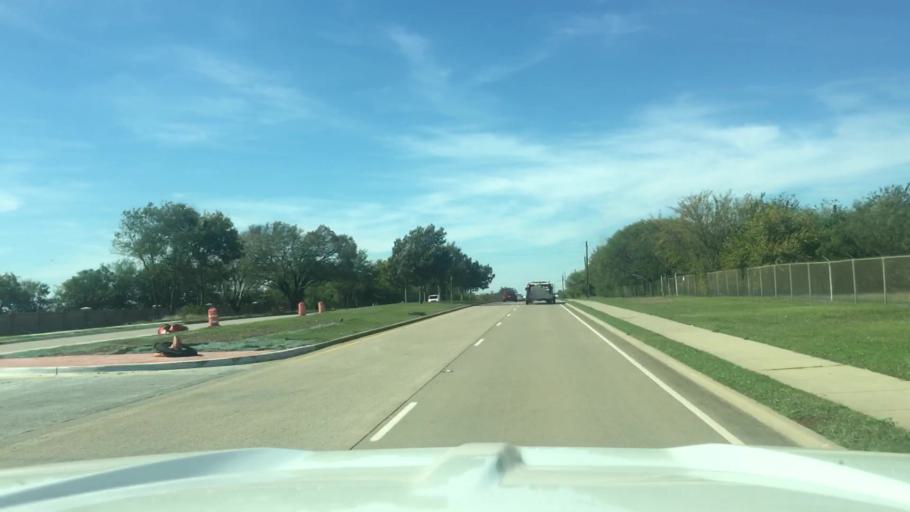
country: US
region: Texas
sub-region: Denton County
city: Denton
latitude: 33.2523
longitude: -97.1551
